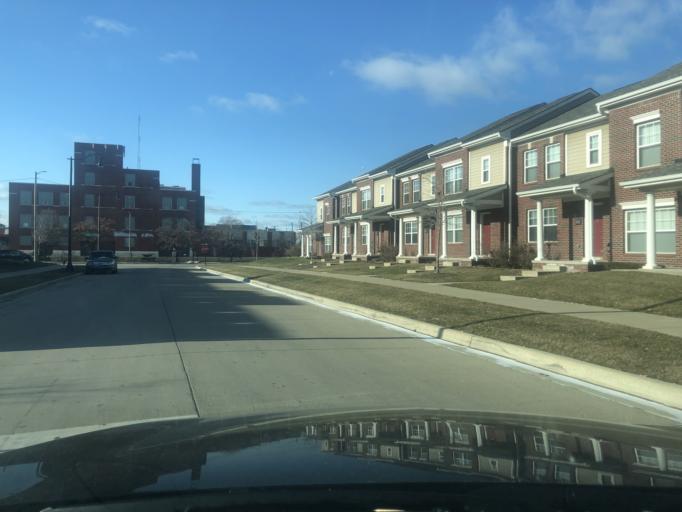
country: US
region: Michigan
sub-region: Wayne County
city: Detroit
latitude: 42.3423
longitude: -83.0663
